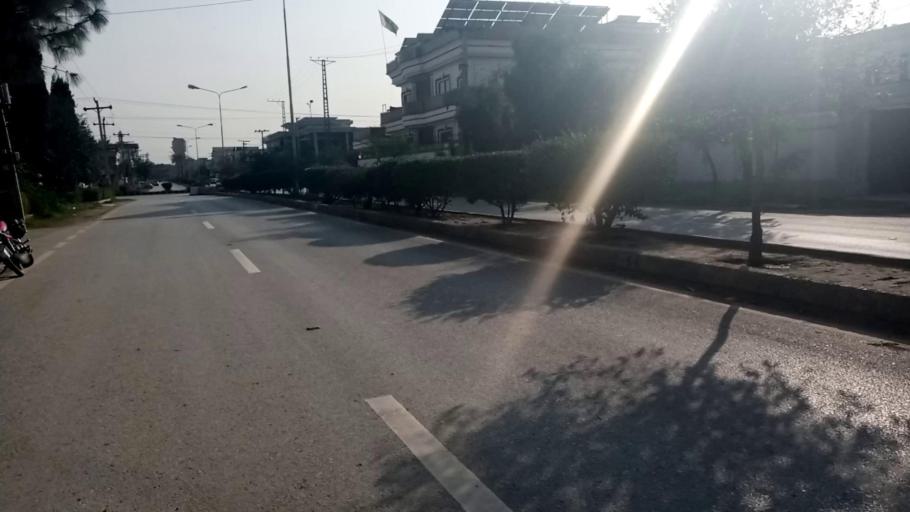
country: PK
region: Khyber Pakhtunkhwa
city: Peshawar
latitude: 33.9898
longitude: 71.4458
